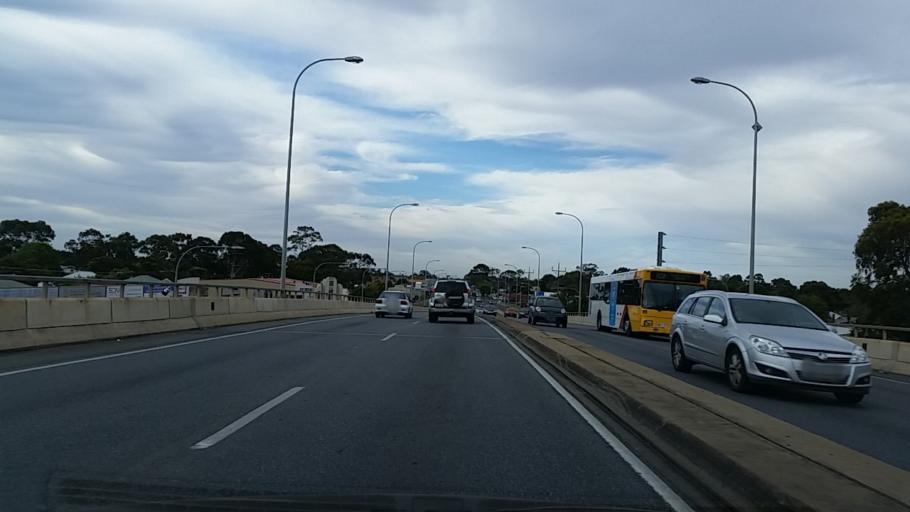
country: AU
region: South Australia
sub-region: Mitcham
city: Clarence Gardens
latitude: -34.9670
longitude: 138.5729
